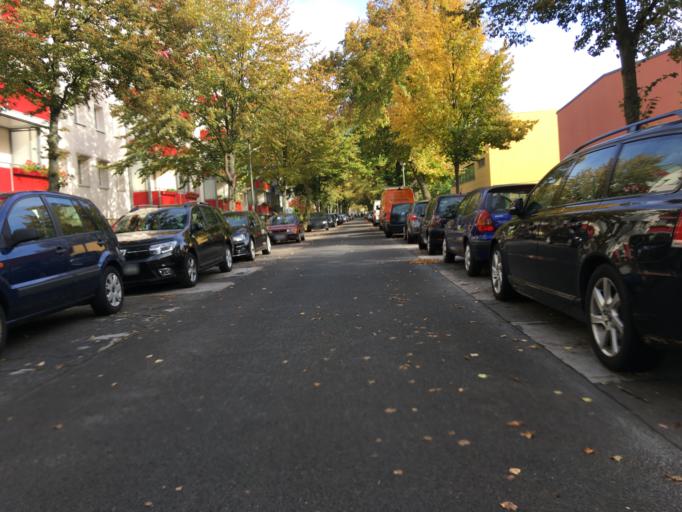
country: DE
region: Berlin
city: Pankow
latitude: 52.5604
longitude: 13.4074
